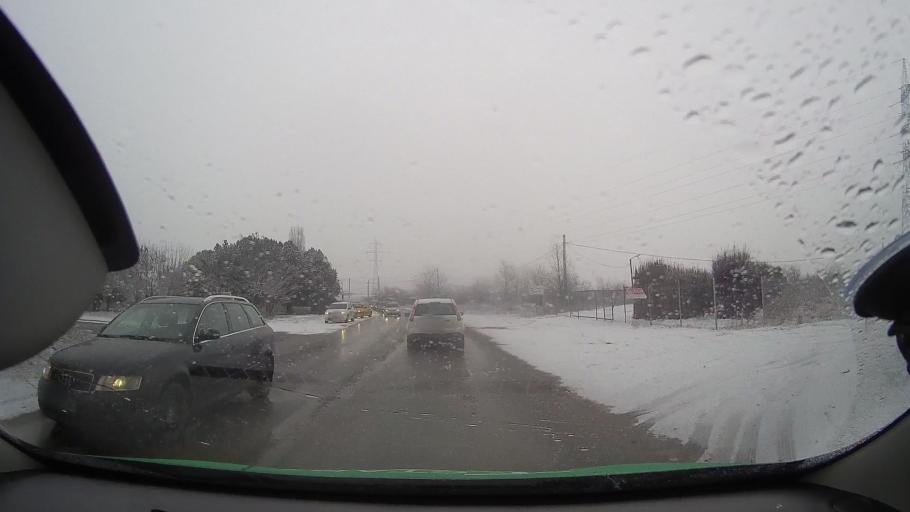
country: RO
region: Alba
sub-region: Municipiul Aiud
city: Aiud
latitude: 46.3054
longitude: 23.7338
